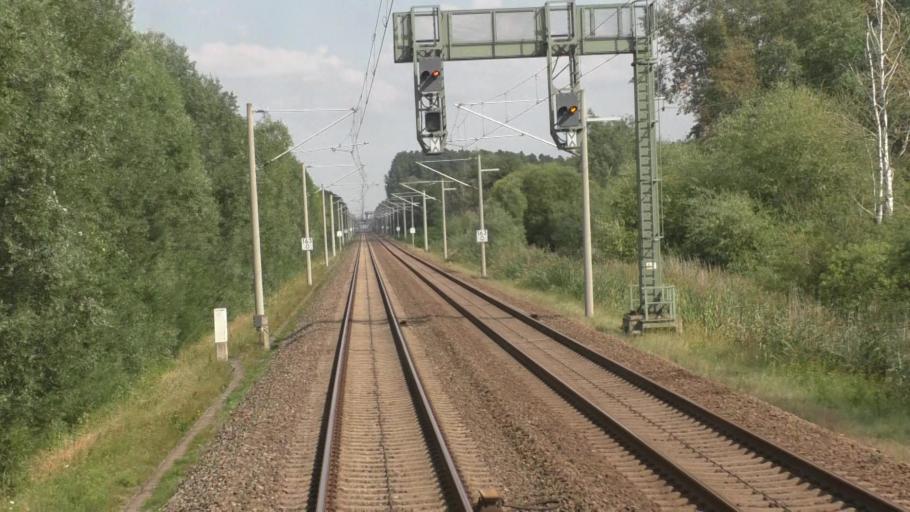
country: DE
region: Brandenburg
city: Nennhausen
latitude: 52.6016
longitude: 12.4682
